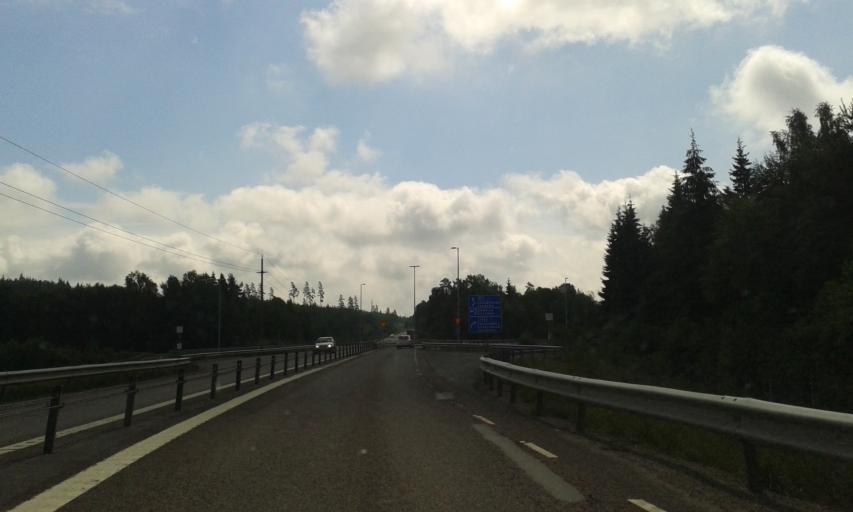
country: SE
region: Vaestra Goetaland
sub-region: Tranemo Kommun
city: Langhem
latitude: 57.6095
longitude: 13.1367
